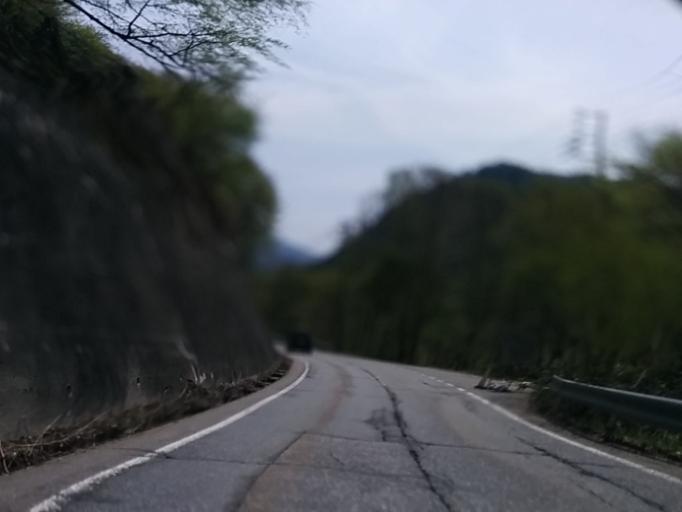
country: JP
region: Gifu
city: Takayama
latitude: 36.2107
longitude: 137.5471
